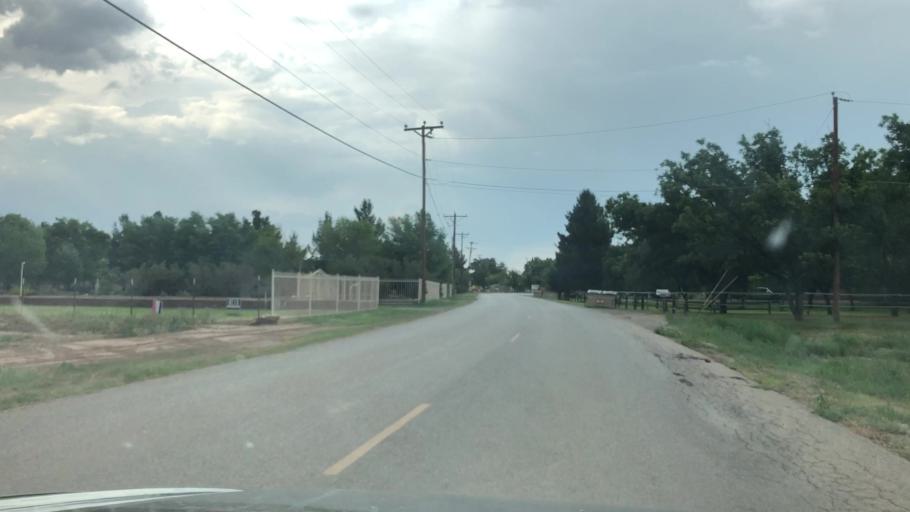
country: US
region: Texas
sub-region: El Paso County
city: Canutillo
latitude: 31.9031
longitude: -106.6393
